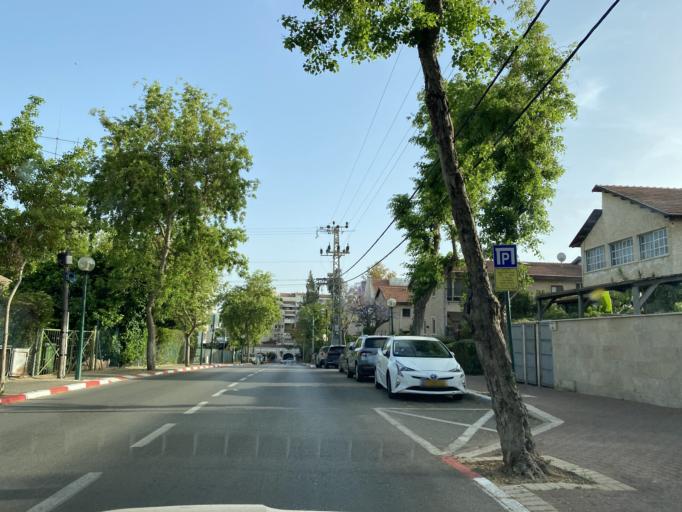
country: IL
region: Central District
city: Kfar Saba
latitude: 32.1796
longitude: 34.9094
